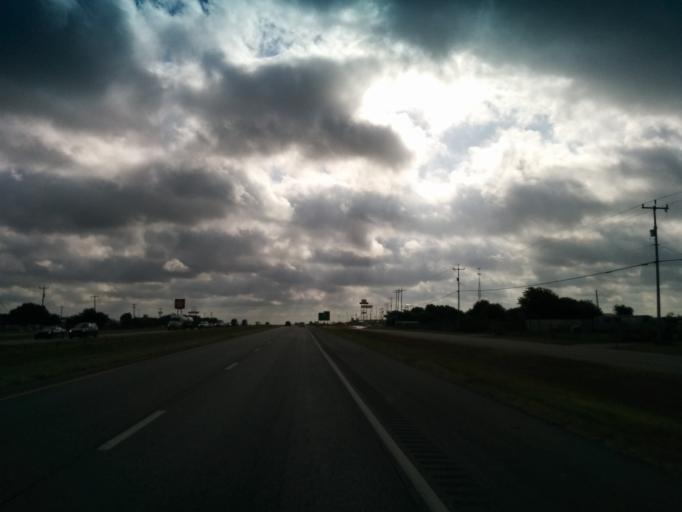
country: US
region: Texas
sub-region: Guadalupe County
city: Cibolo
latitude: 29.4953
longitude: -98.2016
